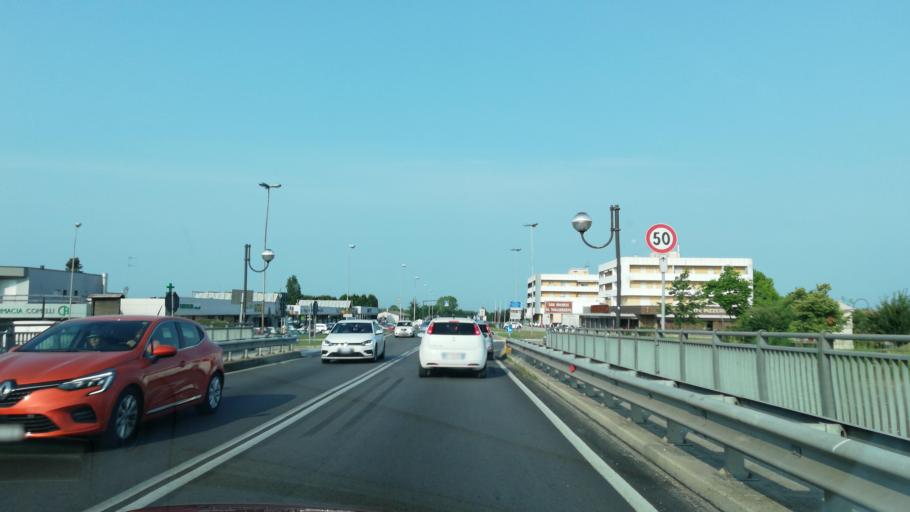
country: IT
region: Veneto
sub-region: Provincia di Venezia
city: San Michele al Tagliamento
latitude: 45.7703
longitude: 12.9963
